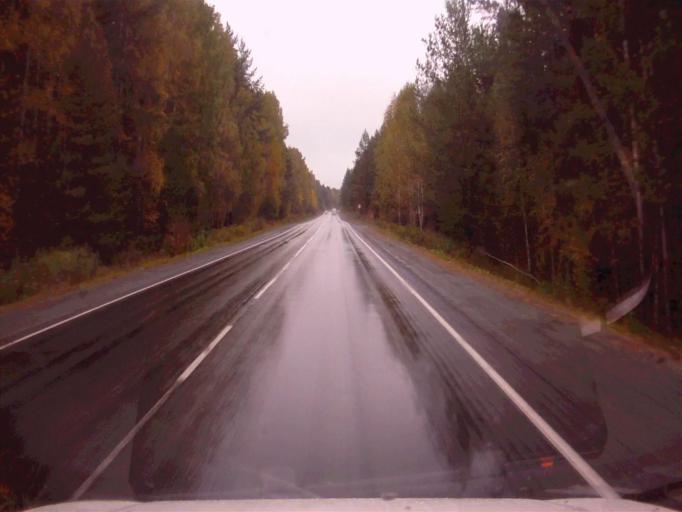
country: RU
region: Chelyabinsk
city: Tayginka
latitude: 55.5516
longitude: 60.6463
